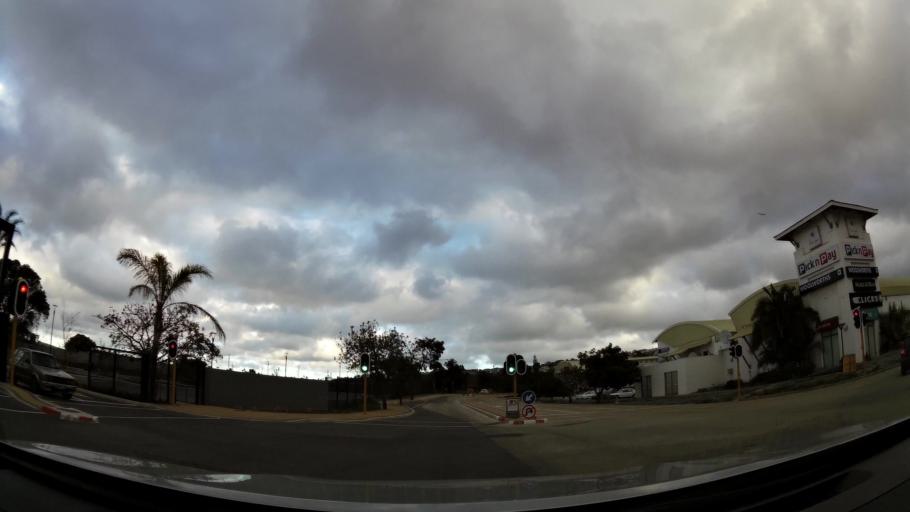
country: ZA
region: Western Cape
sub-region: Eden District Municipality
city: Plettenberg Bay
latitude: -34.0427
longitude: 23.3707
